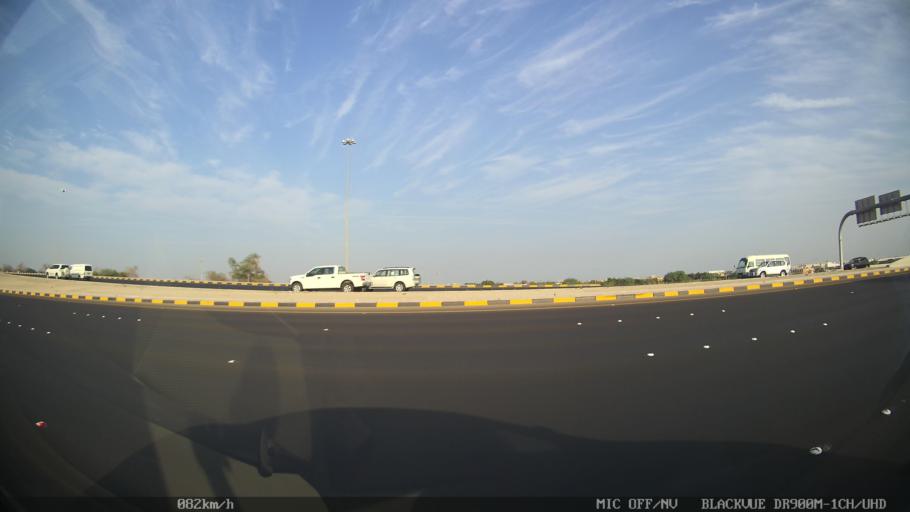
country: KW
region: Al Farwaniyah
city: Janub as Surrah
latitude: 29.2501
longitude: 47.9898
